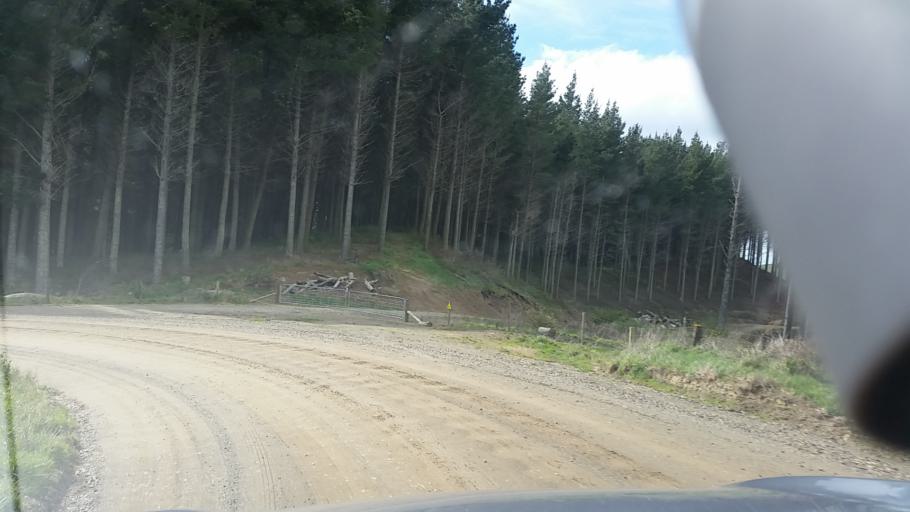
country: NZ
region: Hawke's Bay
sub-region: Napier City
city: Napier
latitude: -39.1939
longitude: 176.9180
